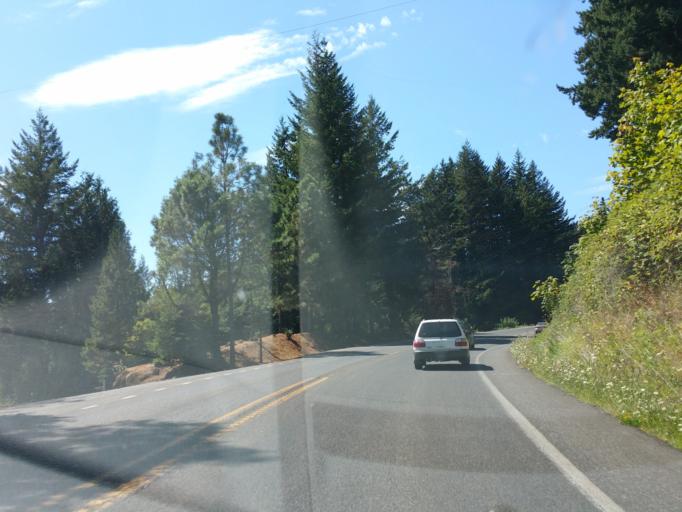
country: US
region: Washington
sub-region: Clark County
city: Washougal
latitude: 45.5913
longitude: -122.1436
